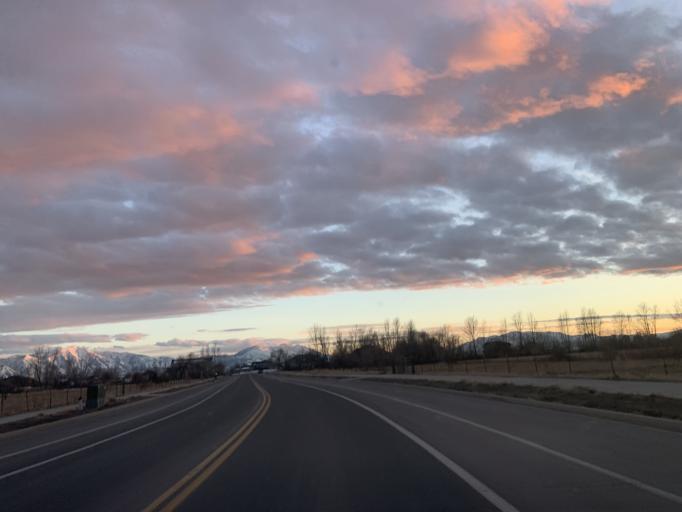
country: US
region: Utah
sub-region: Utah County
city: Provo
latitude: 40.2381
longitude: -111.7133
